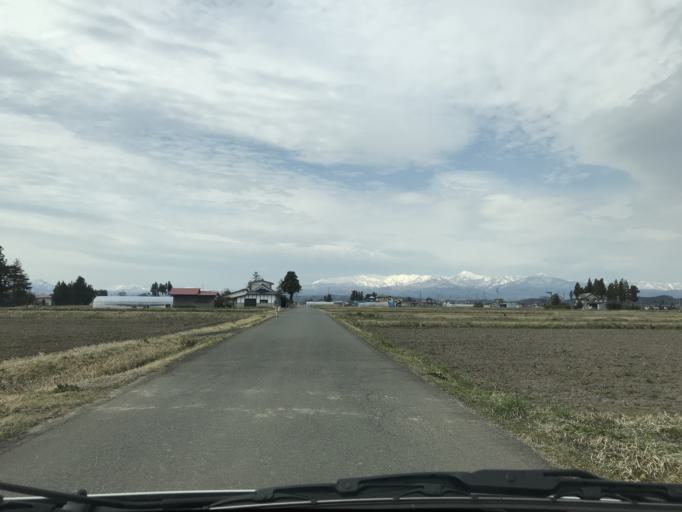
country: JP
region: Iwate
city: Mizusawa
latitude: 39.1493
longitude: 141.1032
